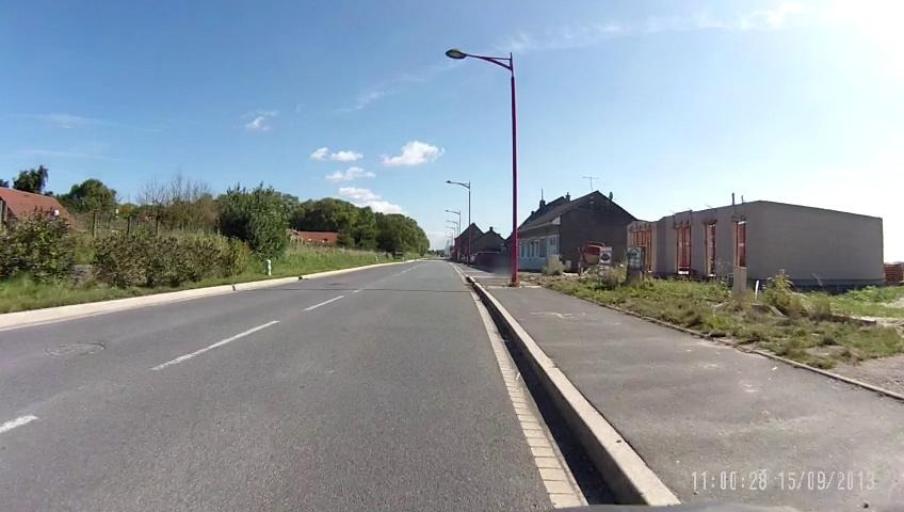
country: FR
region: Nord-Pas-de-Calais
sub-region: Departement du Nord
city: Zuydcoote
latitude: 51.0660
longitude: 2.4947
